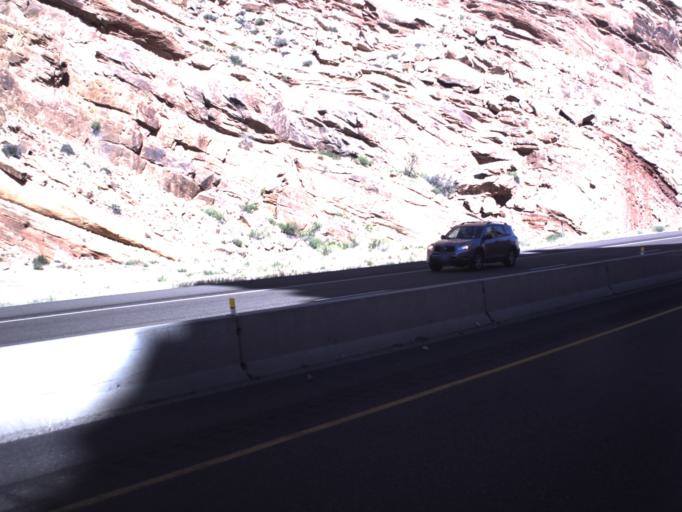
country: US
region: Utah
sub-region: Carbon County
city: East Carbon City
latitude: 38.9224
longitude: -110.4434
